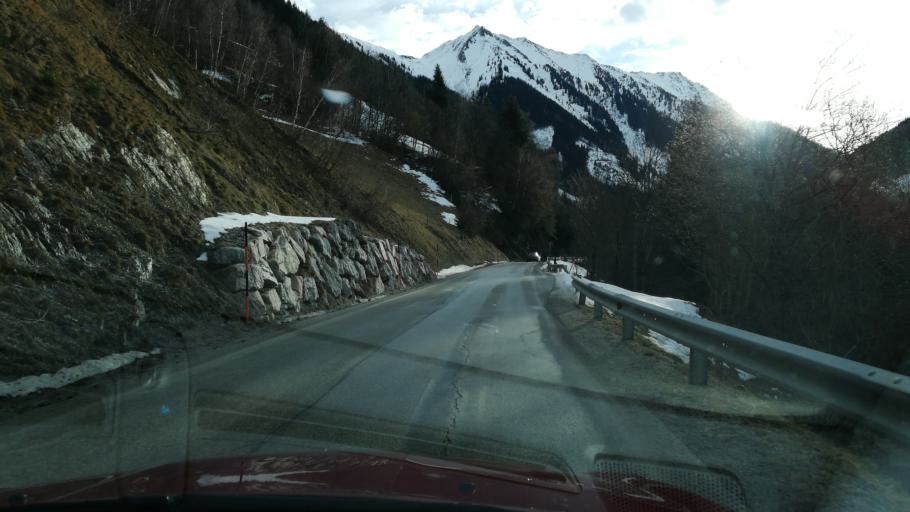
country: AT
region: Styria
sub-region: Politischer Bezirk Liezen
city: Donnersbach
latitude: 47.4377
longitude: 14.1480
